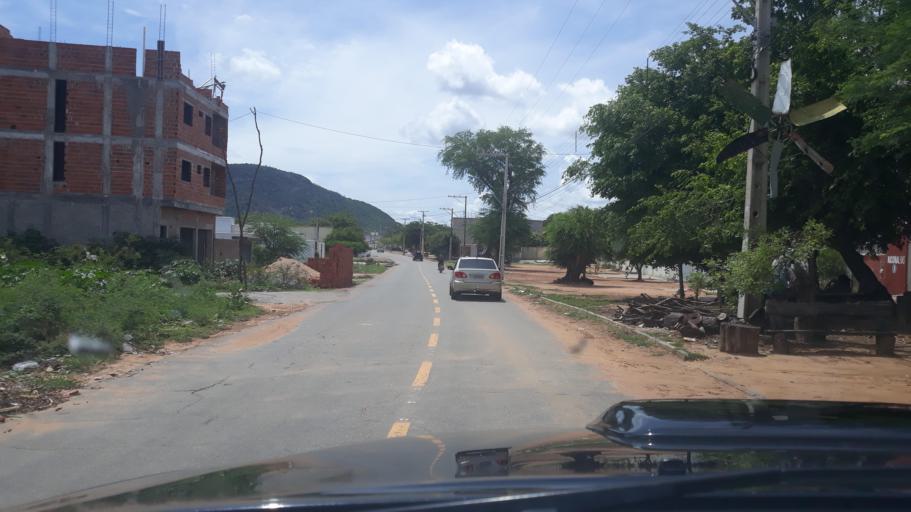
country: BR
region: Bahia
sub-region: Guanambi
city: Guanambi
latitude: -14.2859
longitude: -42.7102
